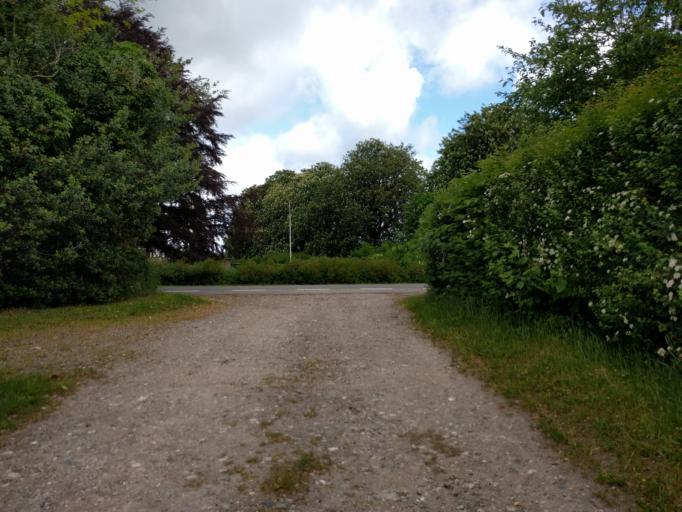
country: DK
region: South Denmark
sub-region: Kerteminde Kommune
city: Langeskov
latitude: 55.4019
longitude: 10.6145
